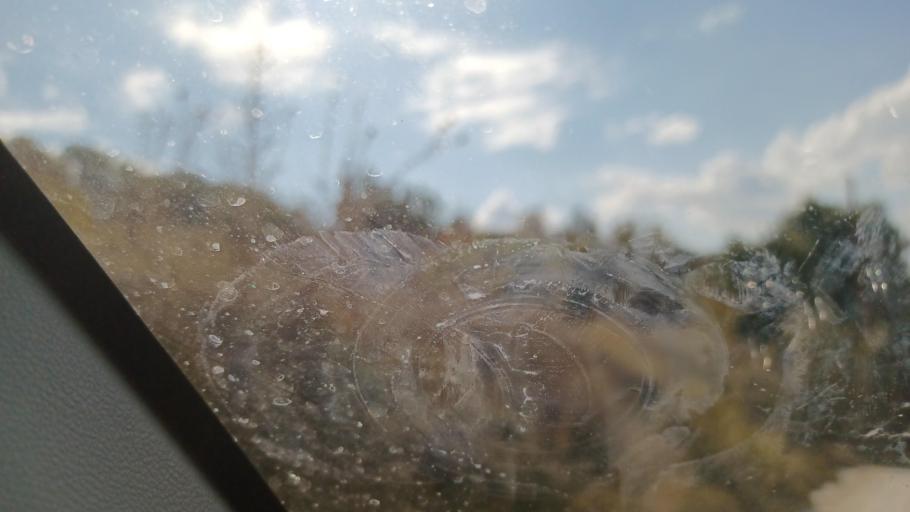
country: CY
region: Pafos
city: Mesogi
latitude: 34.8444
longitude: 32.5738
